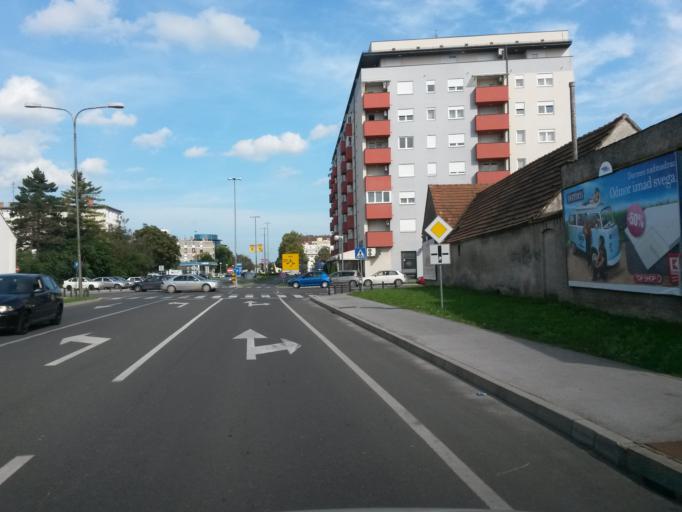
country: HR
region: Varazdinska
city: Varazdin
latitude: 46.2976
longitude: 16.3352
